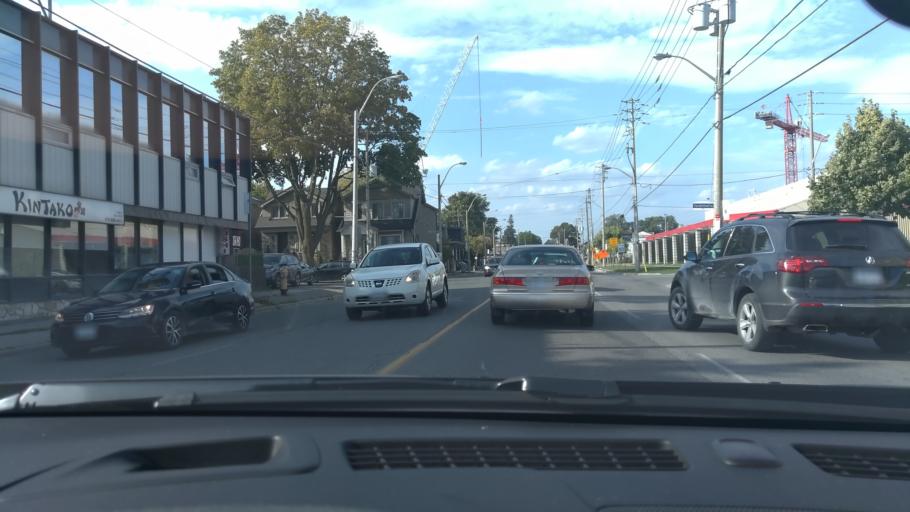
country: CA
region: Ontario
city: Toronto
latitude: 43.7114
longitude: -79.3639
